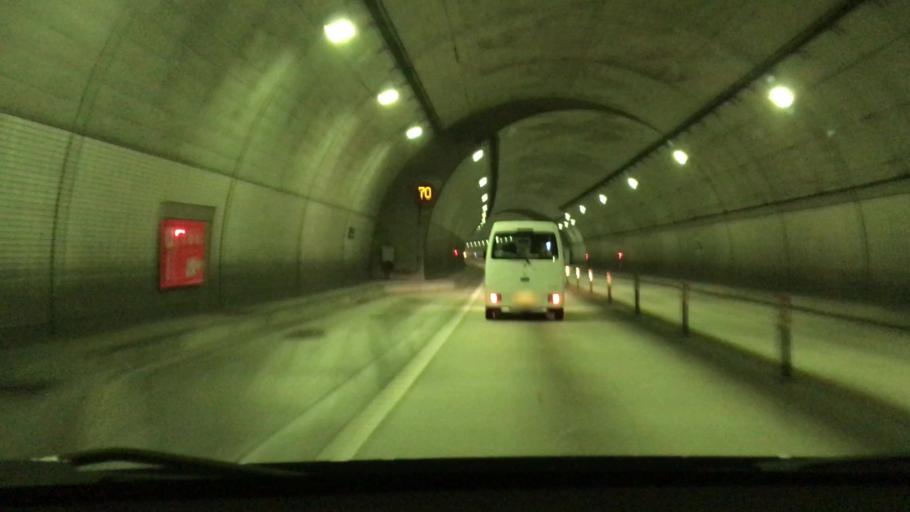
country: JP
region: Nagasaki
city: Sasebo
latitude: 33.0970
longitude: 129.7791
